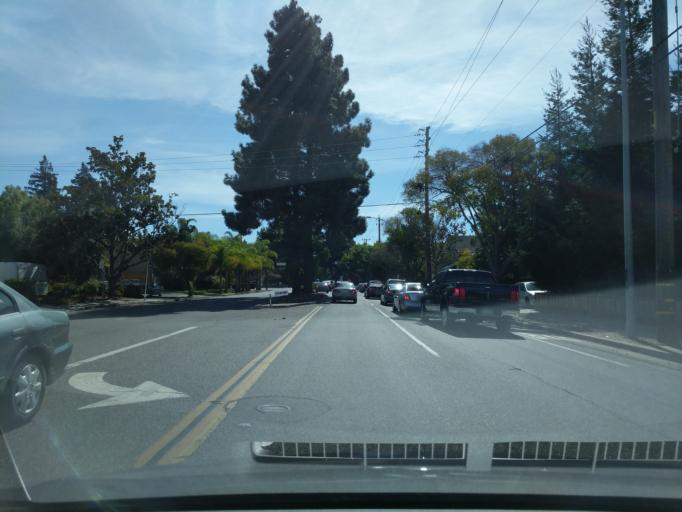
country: US
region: California
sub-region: Santa Clara County
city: Mountain View
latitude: 37.4001
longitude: -122.0993
